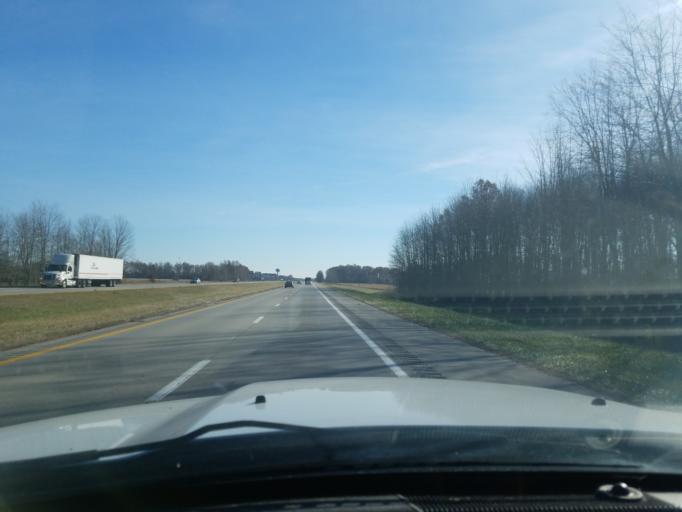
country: US
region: Ohio
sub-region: Brown County
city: Mount Orab
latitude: 39.0499
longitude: -83.9552
